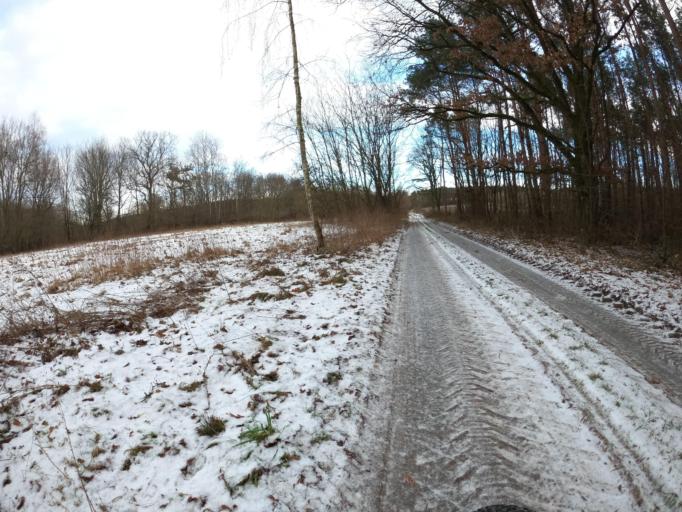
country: PL
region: Lubusz
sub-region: Powiat slubicki
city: Cybinka
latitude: 52.2054
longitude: 14.8480
